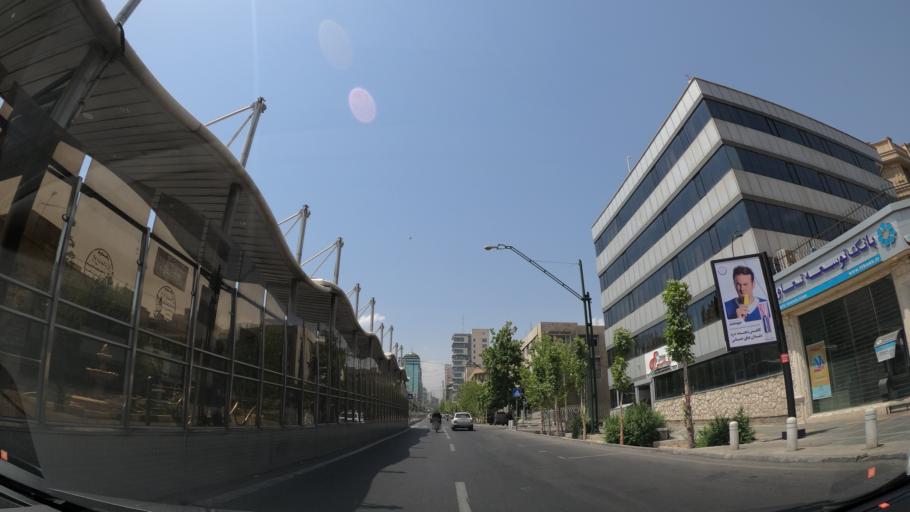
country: IR
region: Tehran
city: Tehran
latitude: 35.7280
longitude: 51.4132
